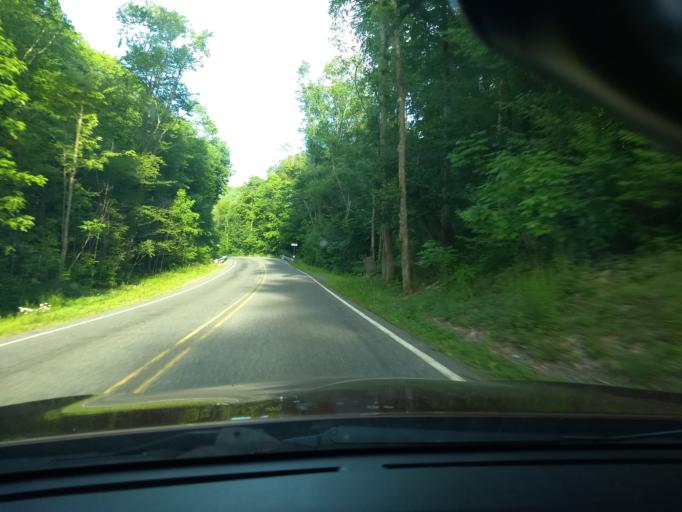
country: US
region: Pennsylvania
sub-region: Cambria County
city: Gallitzin
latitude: 40.4967
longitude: -78.4975
